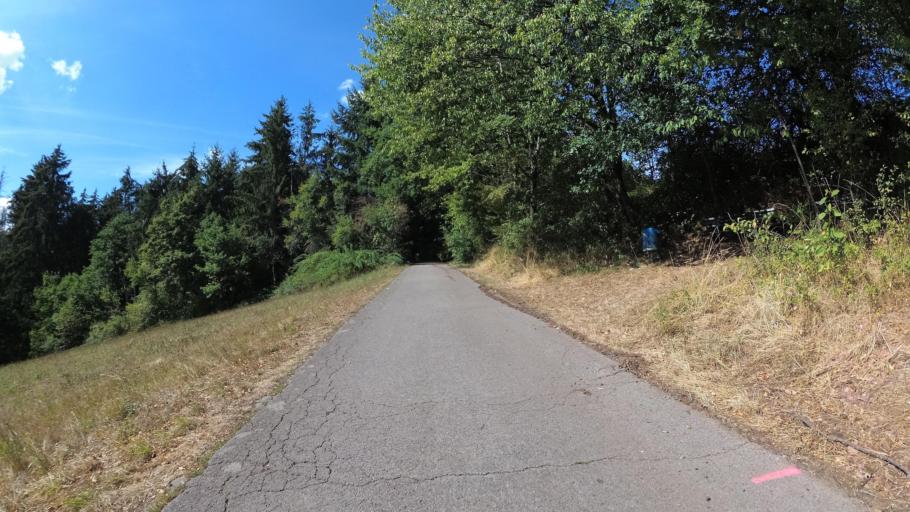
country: DE
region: Saarland
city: Mainzweiler
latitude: 49.4161
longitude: 7.0789
